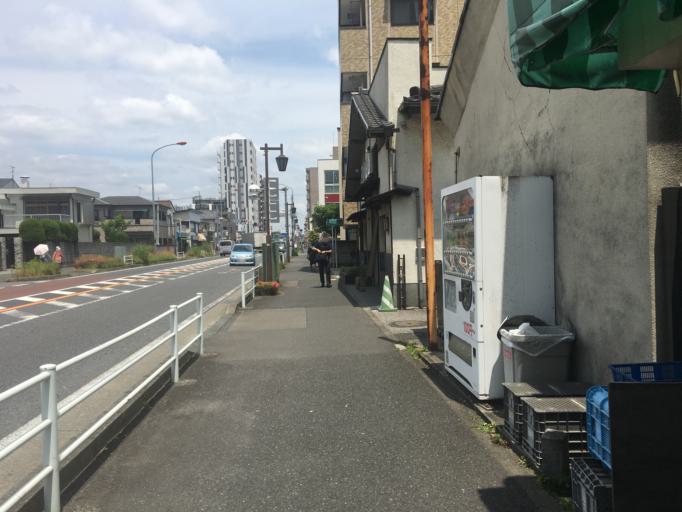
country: JP
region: Saitama
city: Shimotoda
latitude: 35.8129
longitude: 139.6825
